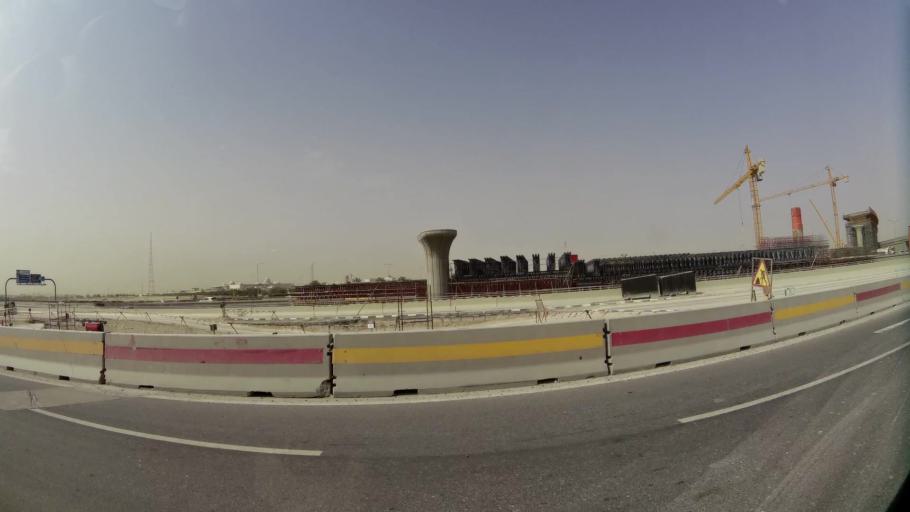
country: QA
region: Baladiyat ad Dawhah
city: Doha
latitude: 25.2939
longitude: 51.4759
